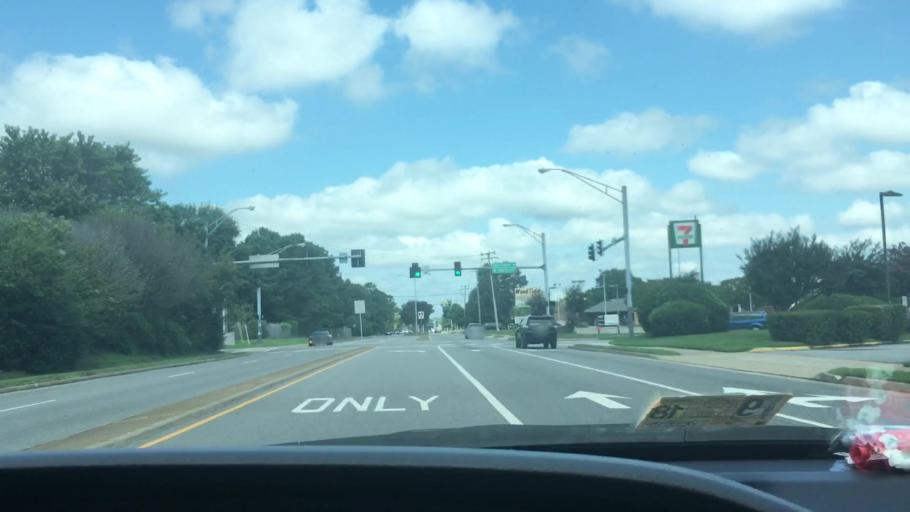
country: US
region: Virginia
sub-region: City of Chesapeake
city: Chesapeake
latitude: 36.8106
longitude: -76.1382
